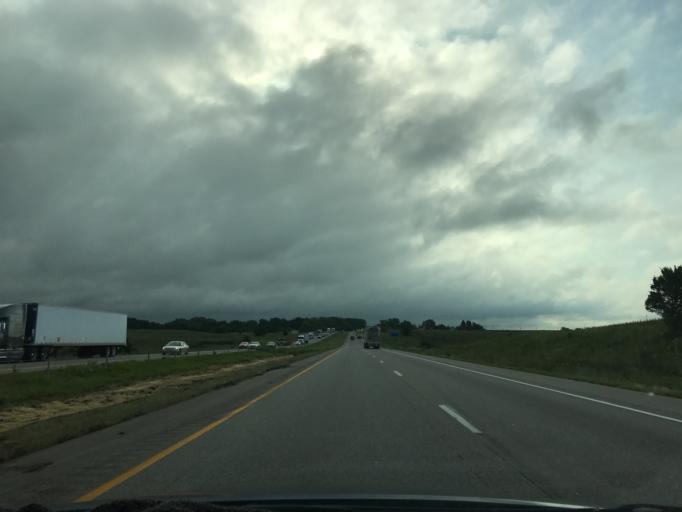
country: US
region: Iowa
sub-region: Muscatine County
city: West Liberty
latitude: 41.6583
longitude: -91.2048
